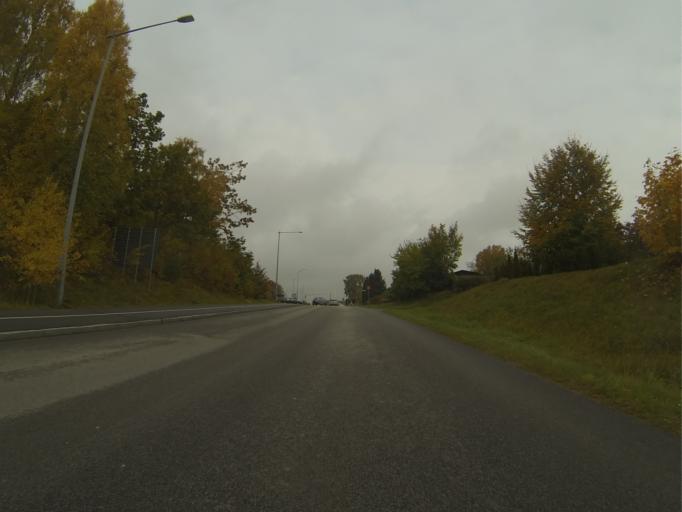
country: SE
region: Skane
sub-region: Sjobo Kommun
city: Sjoebo
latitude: 55.6260
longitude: 13.7051
